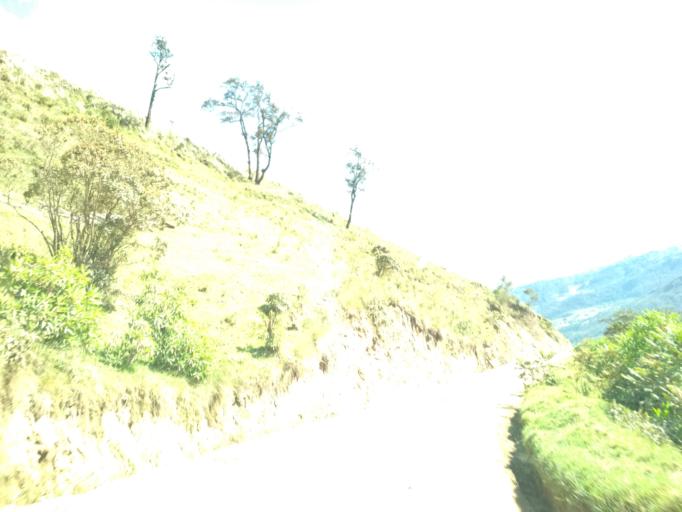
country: CO
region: Cauca
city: Jambalo
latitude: 2.6986
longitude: -76.3275
